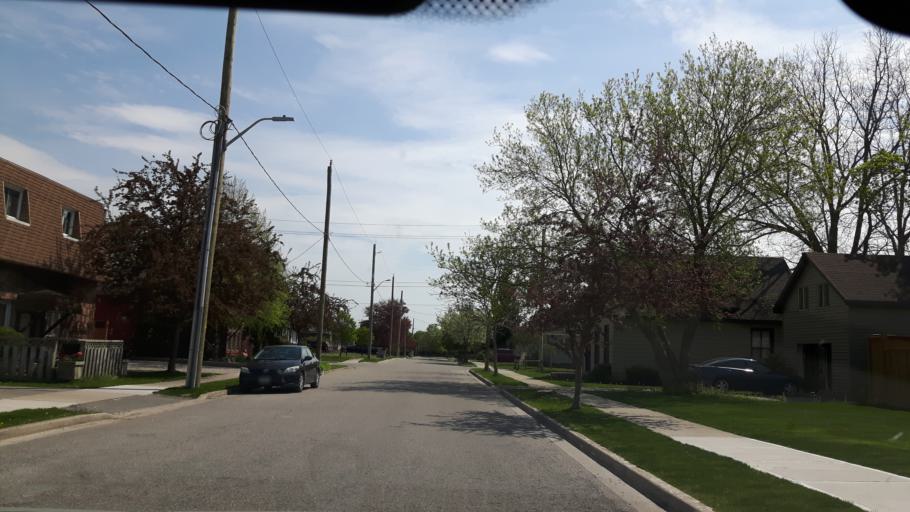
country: CA
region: Ontario
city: Goderich
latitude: 43.7380
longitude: -81.7179
